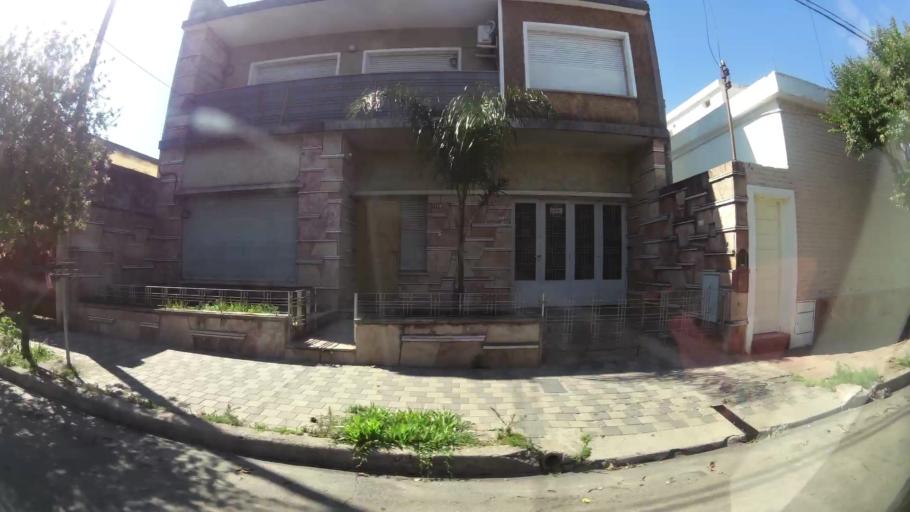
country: AR
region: Cordoba
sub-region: Departamento de Capital
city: Cordoba
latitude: -31.4146
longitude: -64.1597
